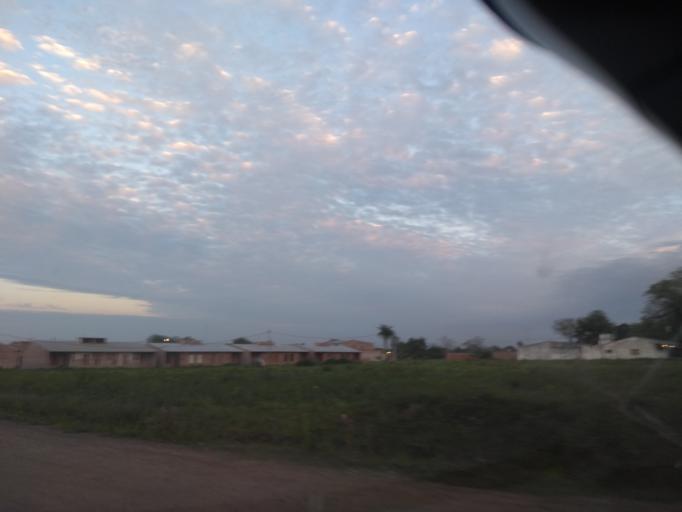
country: AR
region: Chaco
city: Fontana
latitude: -27.4080
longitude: -59.0494
